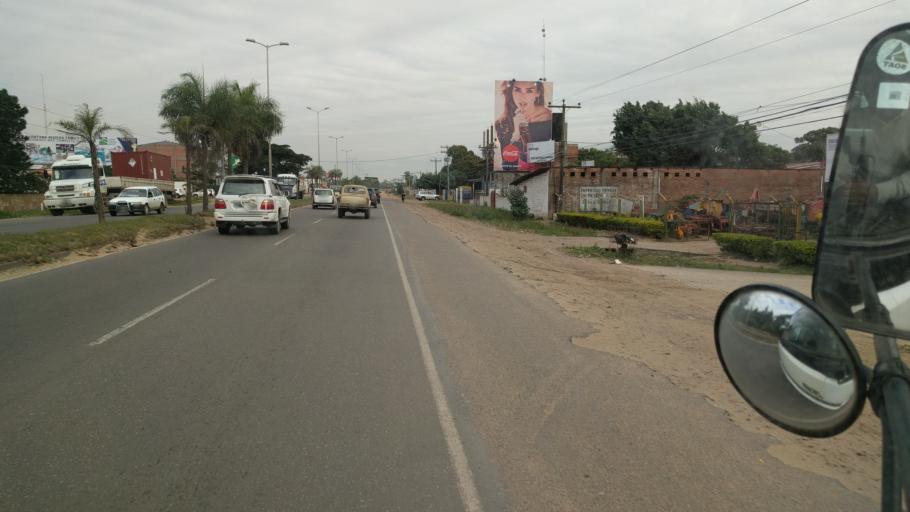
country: BO
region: Santa Cruz
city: Santa Cruz de la Sierra
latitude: -17.7028
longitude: -63.1598
